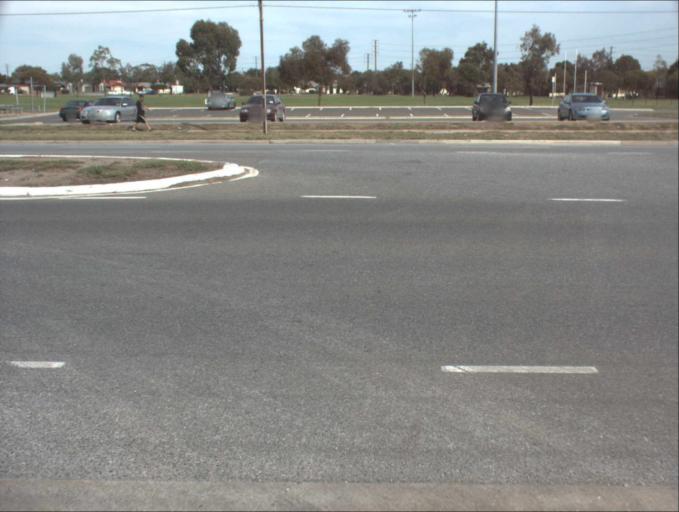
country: AU
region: South Australia
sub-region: Port Adelaide Enfield
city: Birkenhead
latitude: -34.8179
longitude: 138.5015
